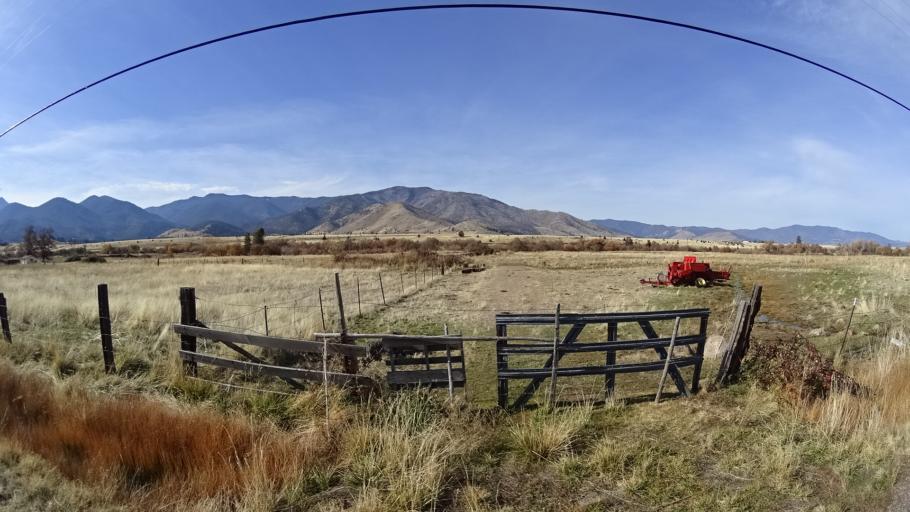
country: US
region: California
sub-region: Siskiyou County
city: Weed
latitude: 41.4668
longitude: -122.4346
